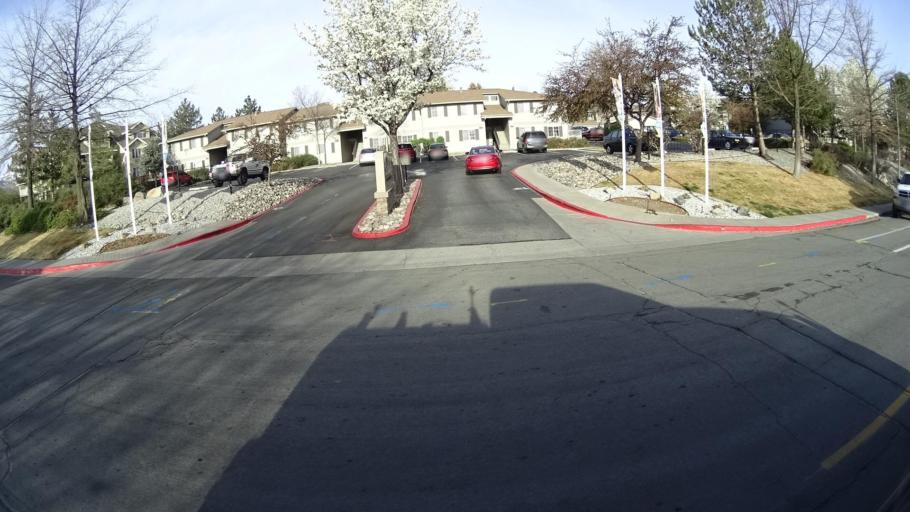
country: US
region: Nevada
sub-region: Washoe County
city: Reno
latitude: 39.5202
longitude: -119.8524
